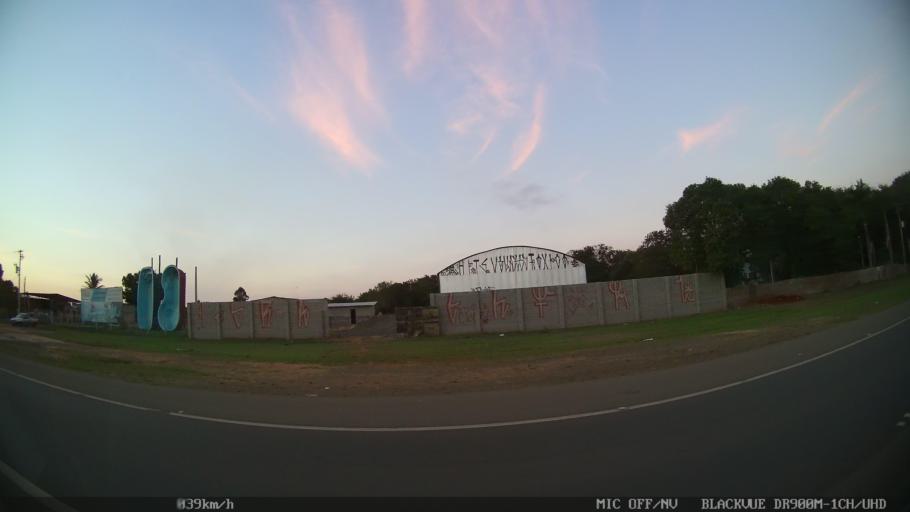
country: BR
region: Sao Paulo
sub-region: Nova Odessa
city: Nova Odessa
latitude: -22.8014
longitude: -47.2846
